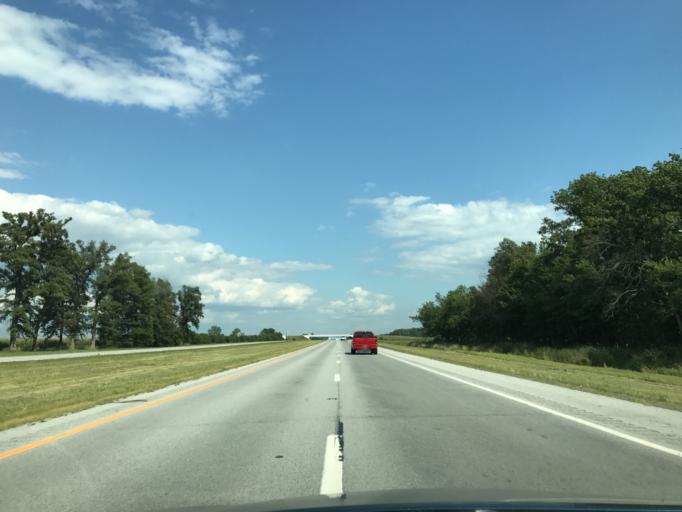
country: US
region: Ohio
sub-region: Allen County
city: Delphos
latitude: 40.8733
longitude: -84.4082
